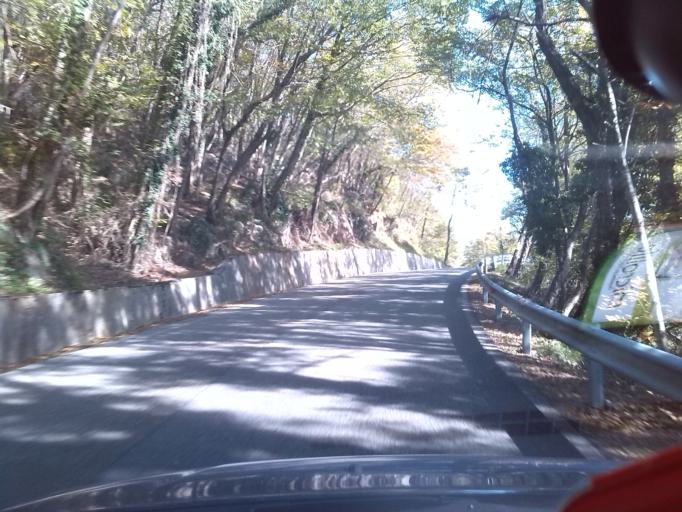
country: IT
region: Friuli Venezia Giulia
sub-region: Provincia di Udine
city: San Pietro al Natisone
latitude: 46.0894
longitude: 13.4862
